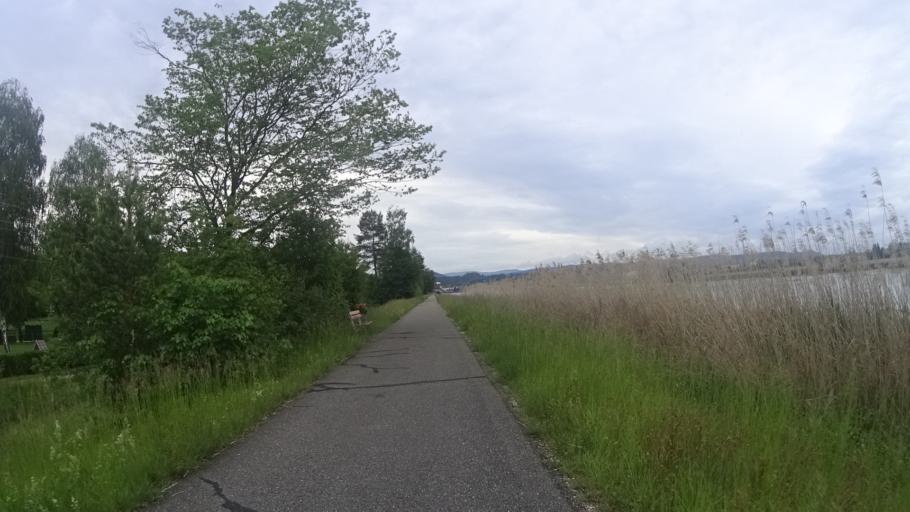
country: CH
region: Aargau
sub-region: Bezirk Zurzach
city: Klingnau
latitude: 47.5833
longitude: 8.2405
